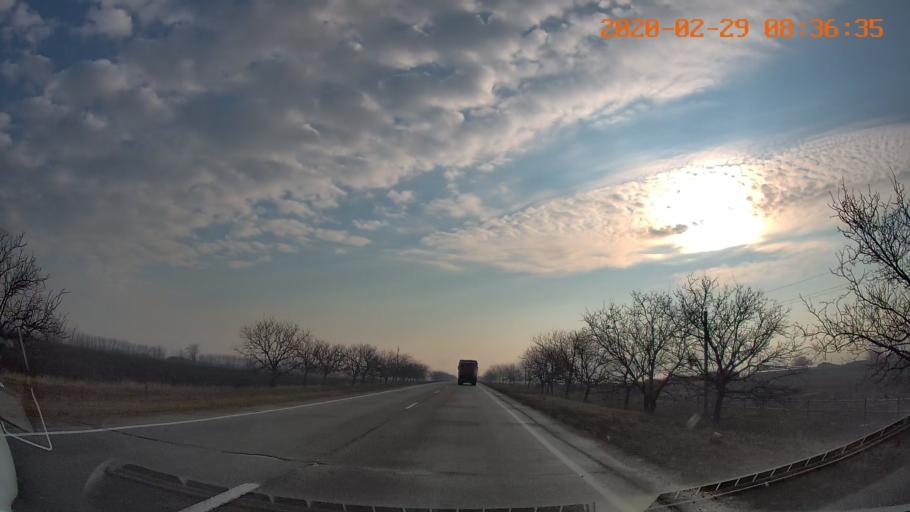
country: MD
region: Anenii Noi
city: Anenii Noi
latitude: 46.9217
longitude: 29.3478
